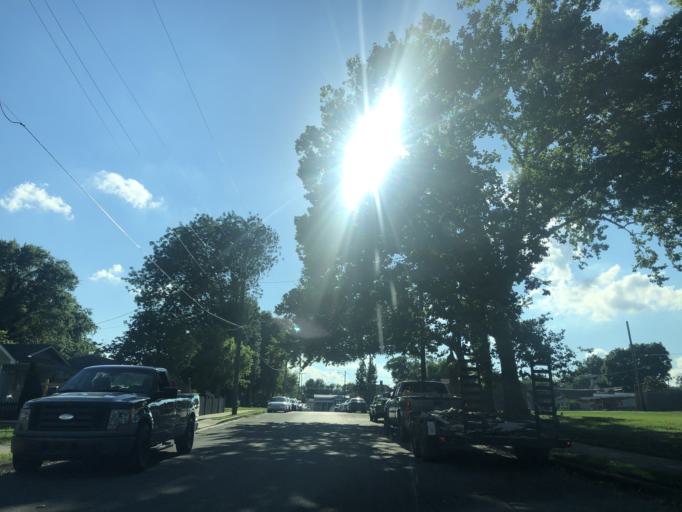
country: US
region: Tennessee
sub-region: Davidson County
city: Nashville
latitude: 36.1847
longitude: -86.7660
